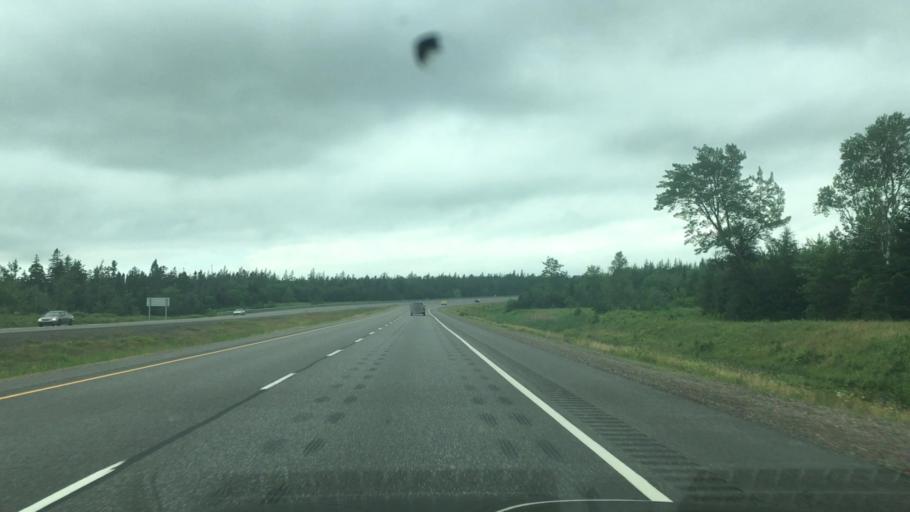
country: CA
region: Nova Scotia
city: Truro
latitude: 45.4314
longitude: -63.5700
